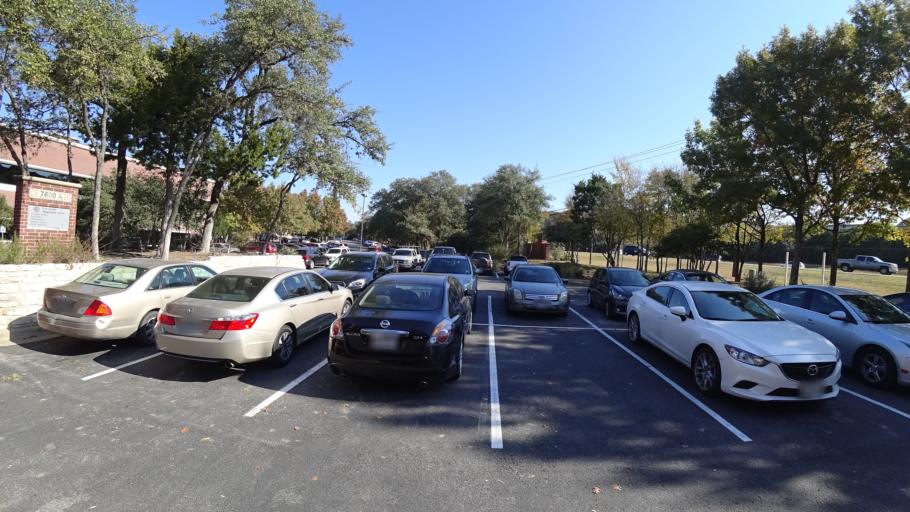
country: US
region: Texas
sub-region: Williamson County
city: Jollyville
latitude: 30.3743
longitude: -97.7835
